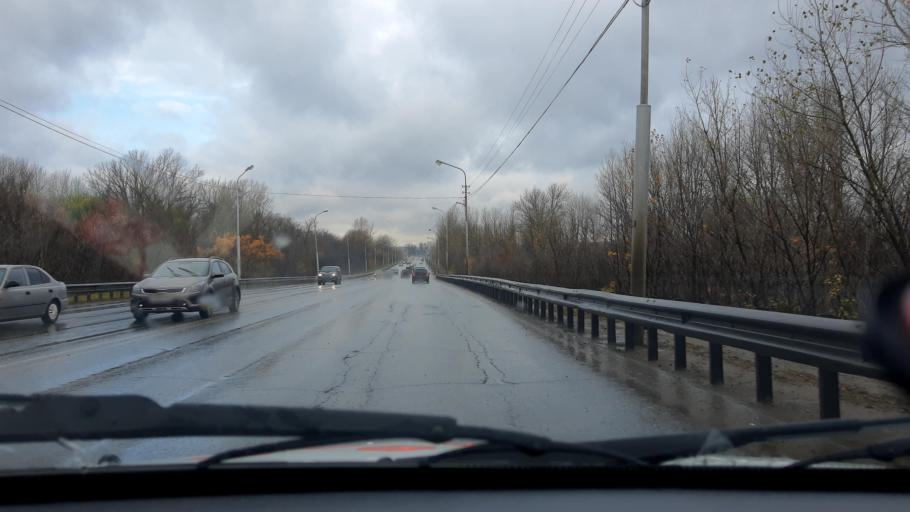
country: RU
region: Bashkortostan
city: Iglino
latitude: 54.7902
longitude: 56.2146
